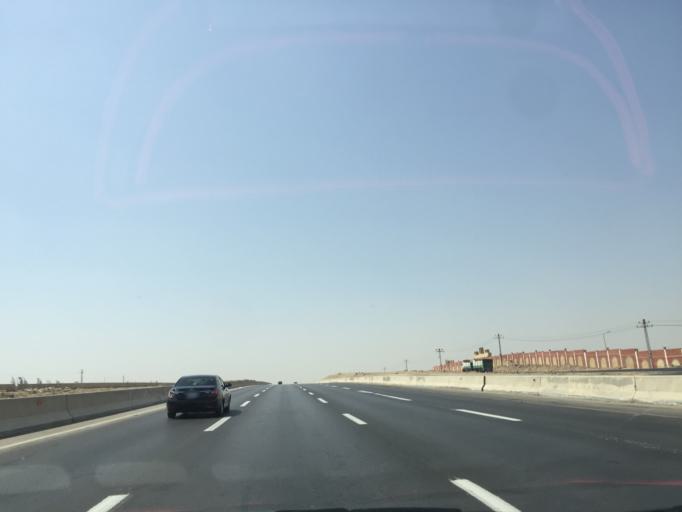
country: EG
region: Al Jizah
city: Awsim
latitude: 30.0860
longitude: 30.9838
